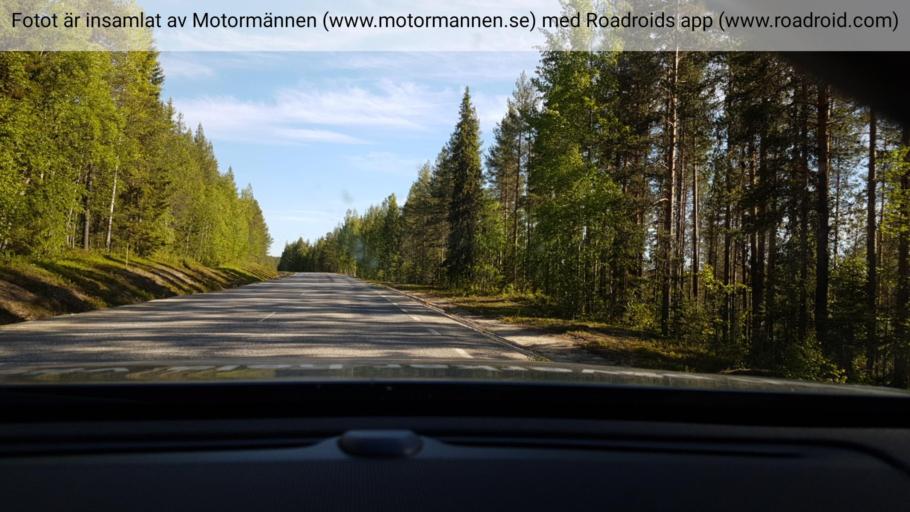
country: SE
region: Vaesterbotten
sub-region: Norsjo Kommun
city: Norsjoe
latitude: 64.6153
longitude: 19.2899
